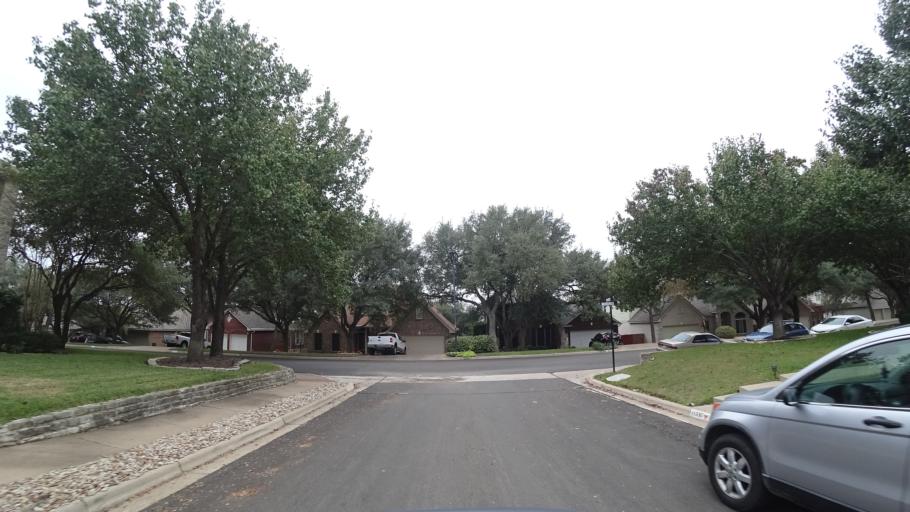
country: US
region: Texas
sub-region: Travis County
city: Shady Hollow
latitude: 30.1825
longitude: -97.8939
